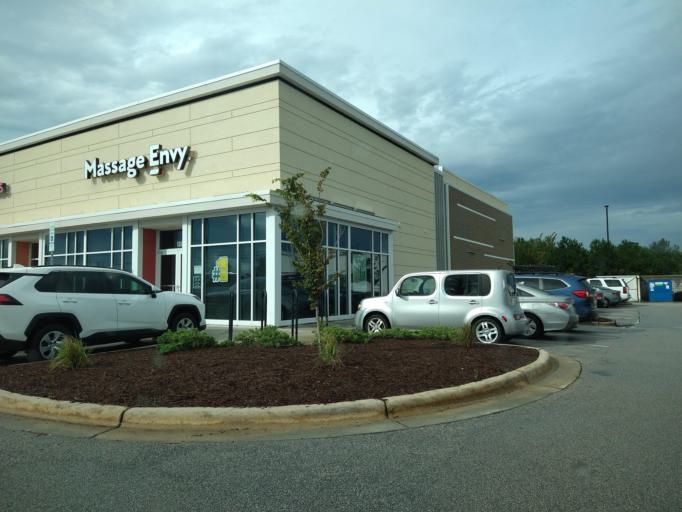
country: US
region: North Carolina
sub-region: Onslow County
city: Pumpkin Center
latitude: 34.7958
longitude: -77.4096
